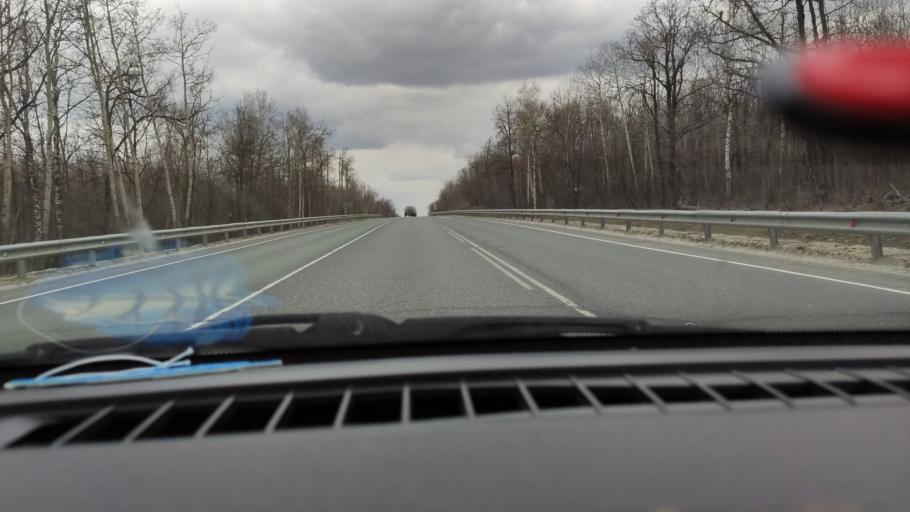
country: RU
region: Saratov
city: Vol'sk
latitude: 52.1102
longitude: 47.3583
